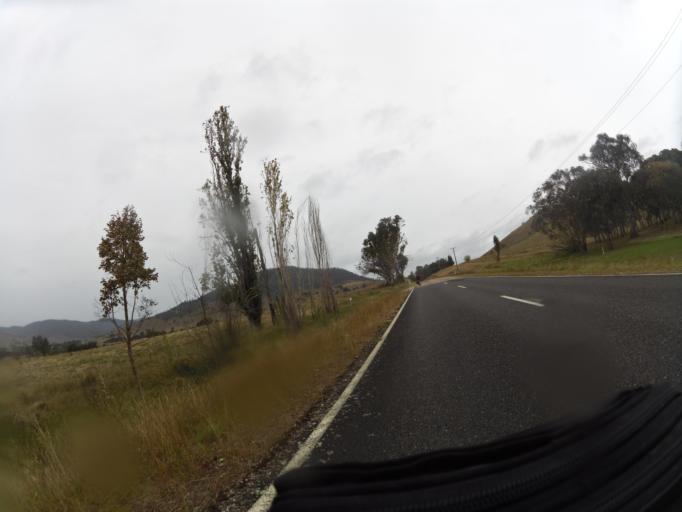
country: AU
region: New South Wales
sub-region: Greater Hume Shire
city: Holbrook
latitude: -36.2126
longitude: 147.7319
